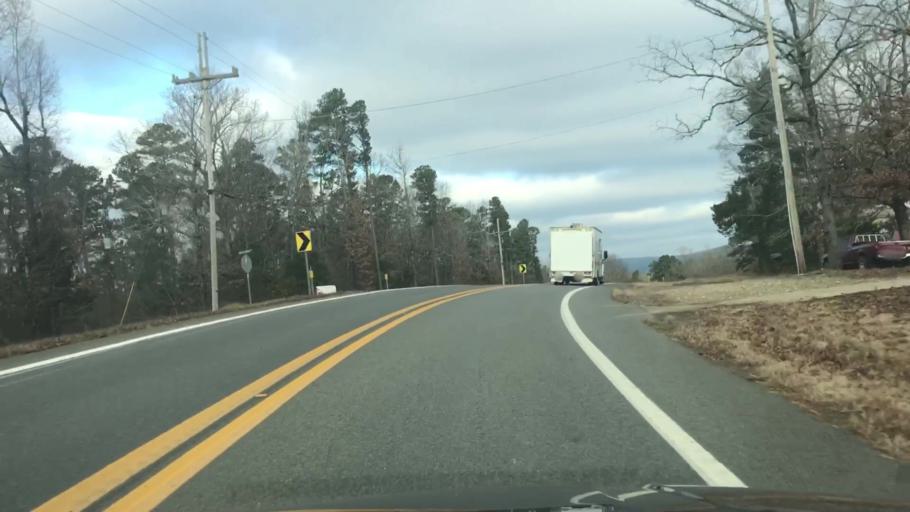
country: US
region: Arkansas
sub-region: Montgomery County
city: Mount Ida
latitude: 34.6196
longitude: -93.7221
